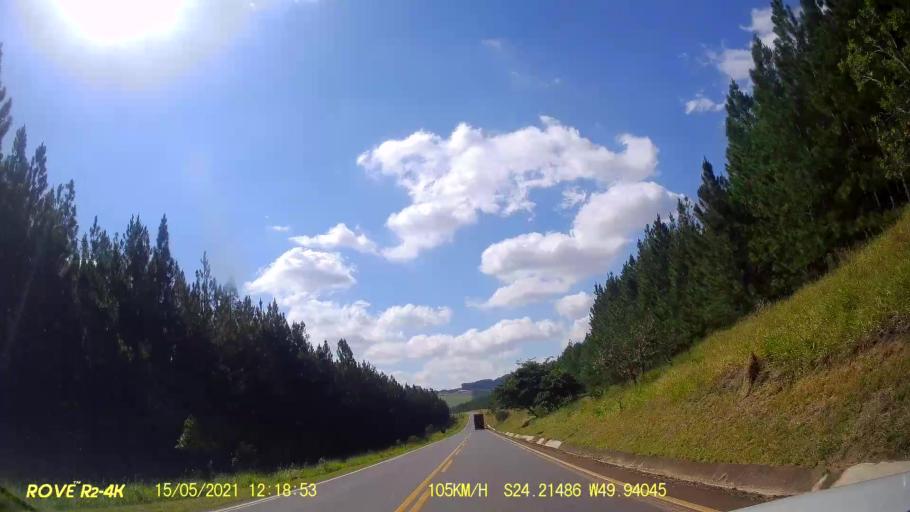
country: BR
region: Parana
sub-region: Jaguariaiva
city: Jaguariaiva
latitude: -24.2158
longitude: -49.9409
